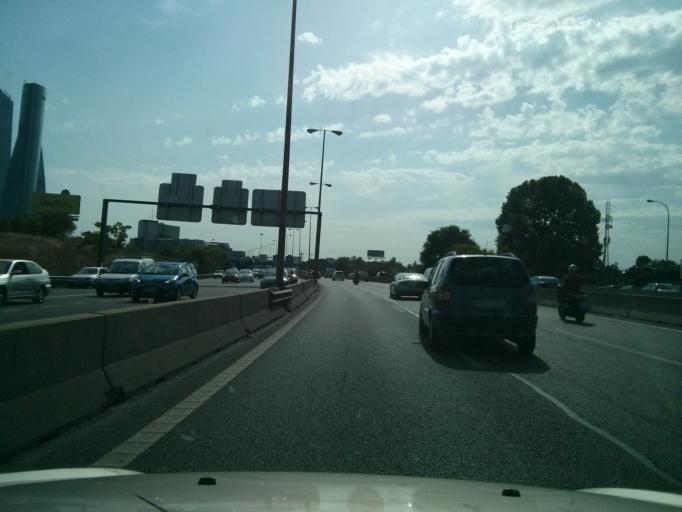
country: ES
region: Madrid
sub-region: Provincia de Madrid
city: Pinar de Chamartin
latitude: 40.4840
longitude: -3.6781
